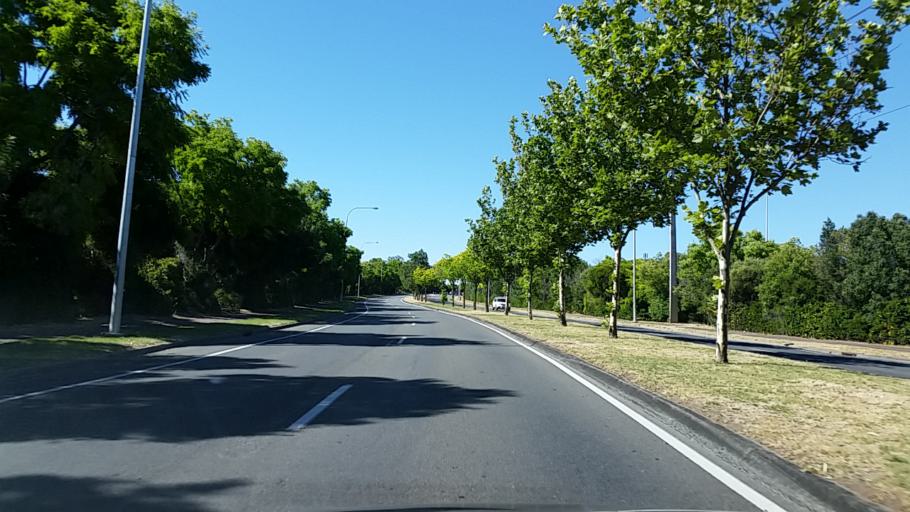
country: AU
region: South Australia
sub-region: Tea Tree Gully
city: Modbury
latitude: -34.8030
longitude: 138.6849
